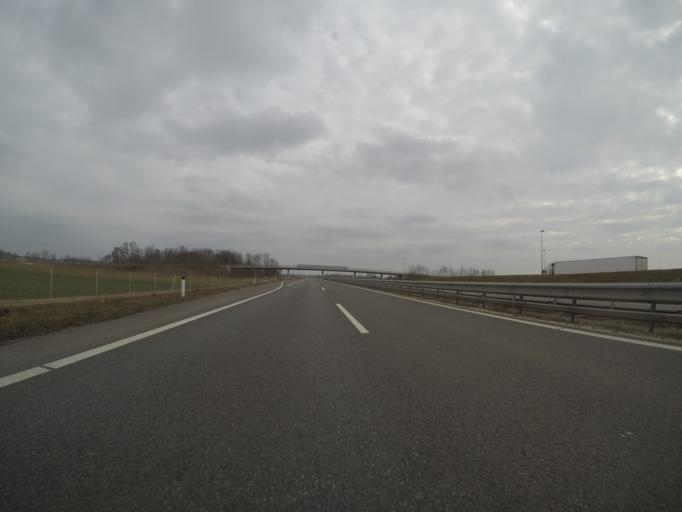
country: SI
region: Turnisce
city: Turnisce
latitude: 46.6205
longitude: 16.2999
